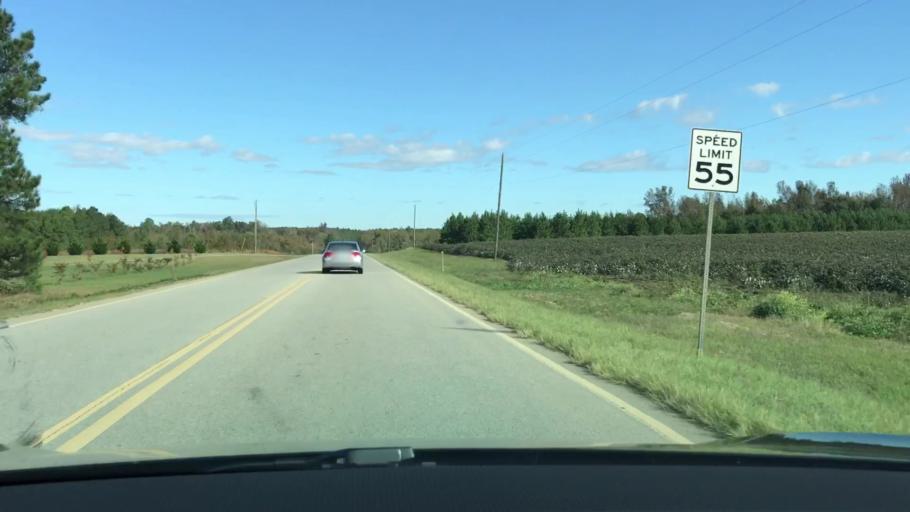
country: US
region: Georgia
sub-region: Jefferson County
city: Wrens
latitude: 33.2298
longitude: -82.4598
